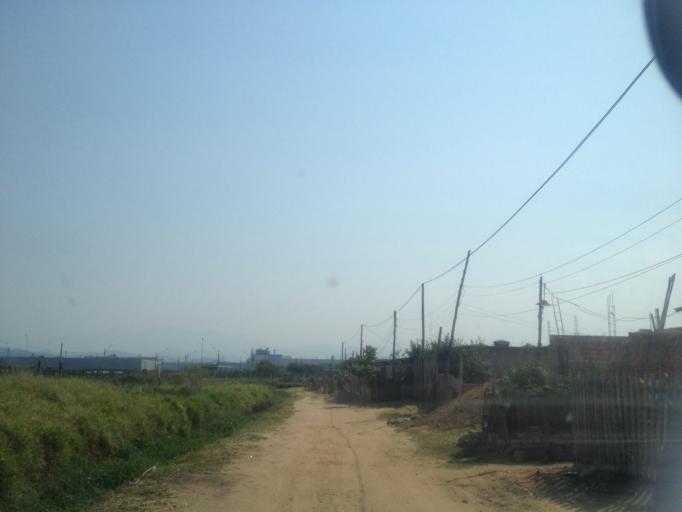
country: BR
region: Rio de Janeiro
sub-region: Porto Real
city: Porto Real
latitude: -22.4311
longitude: -44.3400
